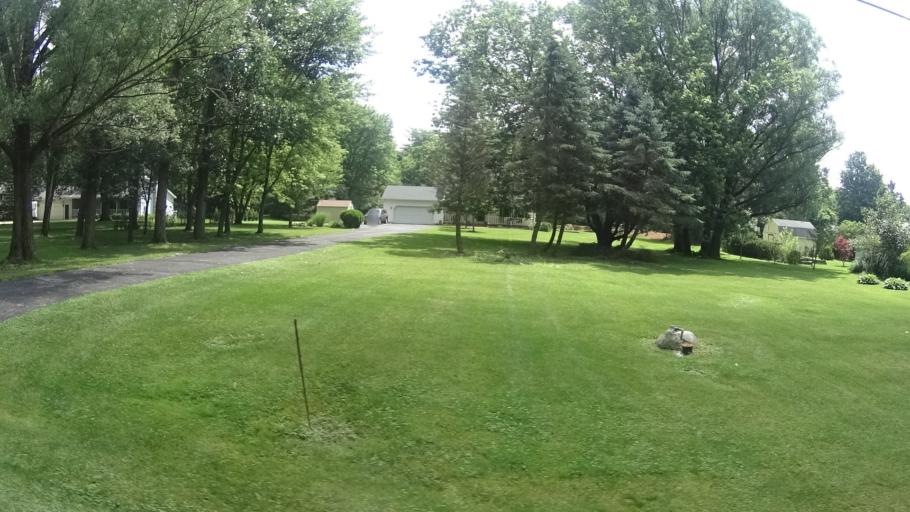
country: US
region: Ohio
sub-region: Huron County
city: Wakeman
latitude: 41.3066
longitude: -82.3633
